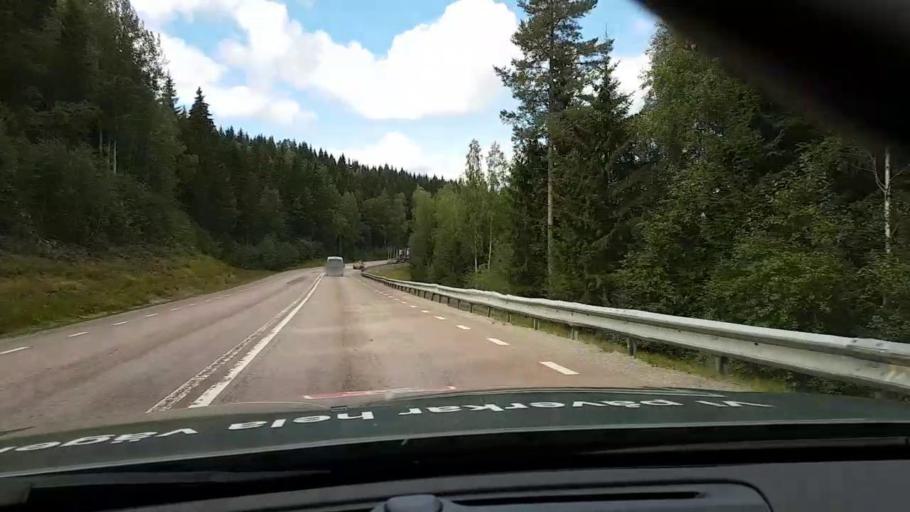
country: SE
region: Vaesternorrland
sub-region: OErnskoeldsviks Kommun
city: Bjasta
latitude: 63.3594
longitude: 18.4707
